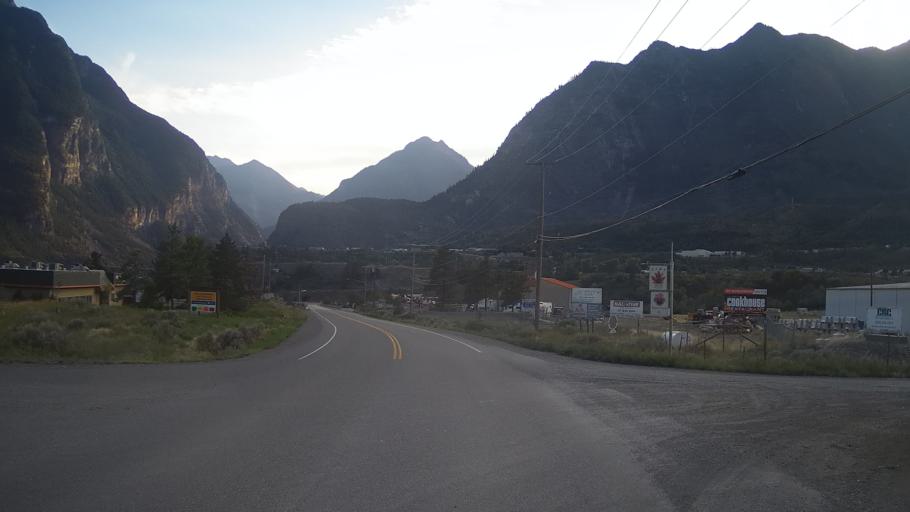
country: CA
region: British Columbia
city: Lillooet
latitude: 50.6857
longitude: -121.9236
